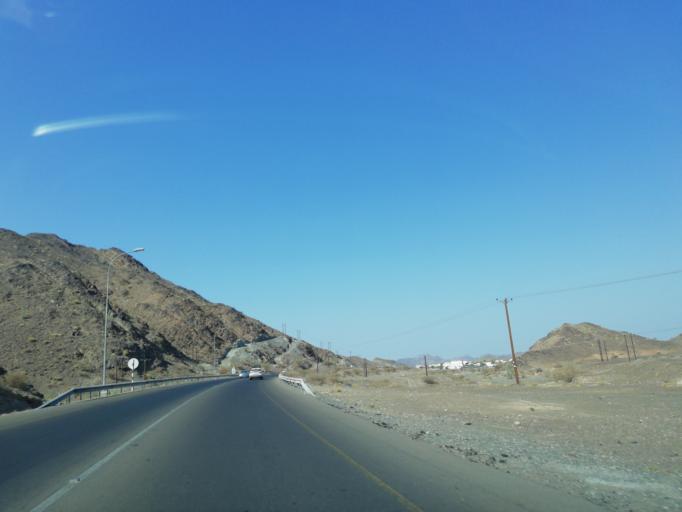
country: OM
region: Ash Sharqiyah
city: Ibra'
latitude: 22.8067
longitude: 58.1679
